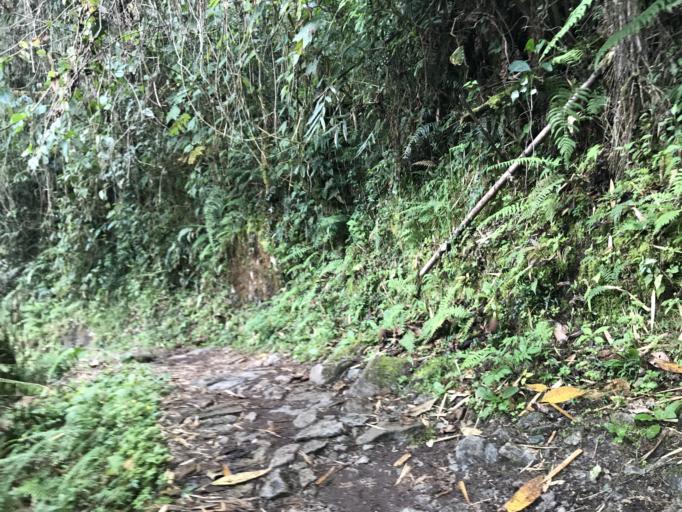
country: PE
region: Cusco
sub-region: Provincia de La Convencion
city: Santa Teresa
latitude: -13.1733
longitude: -72.5346
